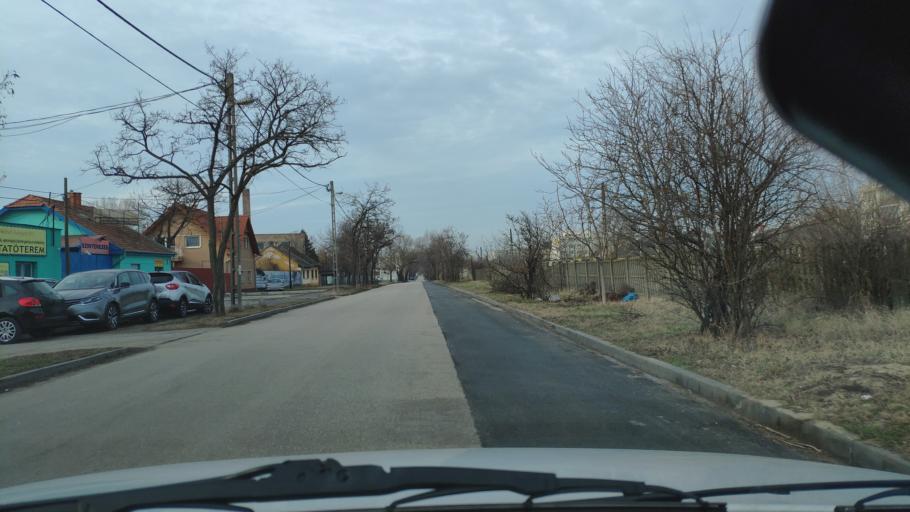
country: HU
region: Budapest
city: Budapest X. keruelet
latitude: 47.4749
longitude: 19.1330
